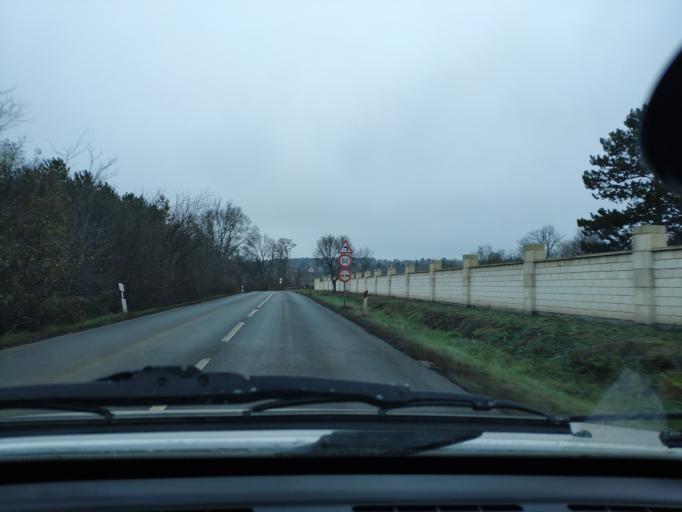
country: HU
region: Pest
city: Soskut
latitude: 47.4321
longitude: 18.8238
